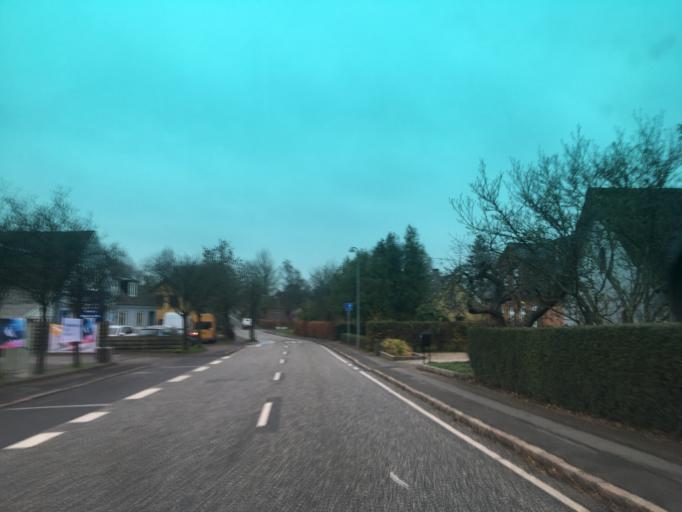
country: DK
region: Zealand
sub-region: Slagelse Kommune
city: Slagelse
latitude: 55.3123
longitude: 11.3954
